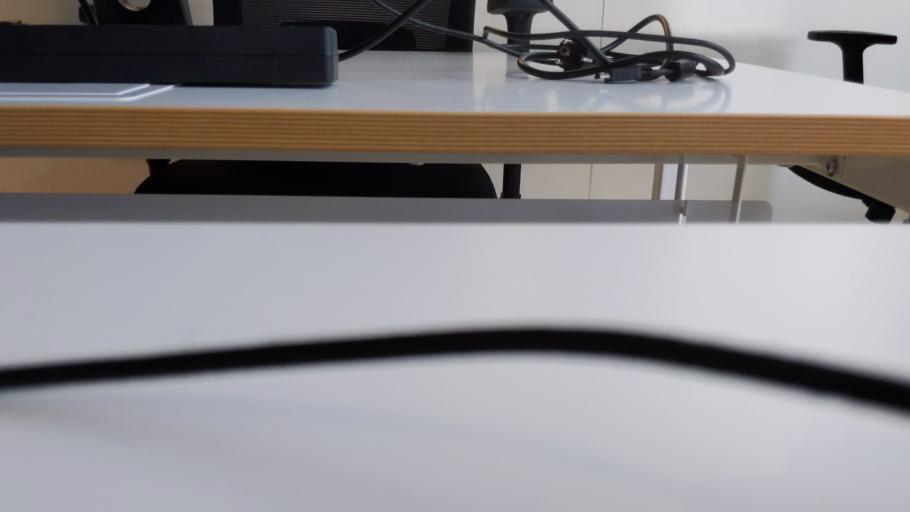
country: RU
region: Moskovskaya
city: Shevlyakovo
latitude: 56.4047
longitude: 36.8972
